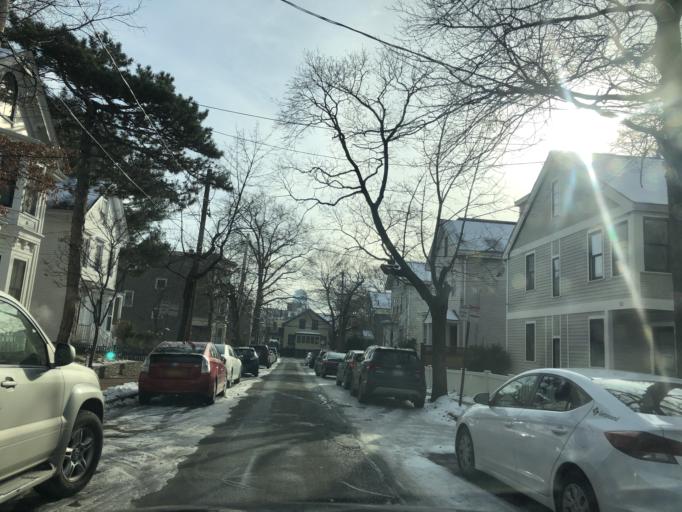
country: US
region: Massachusetts
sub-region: Middlesex County
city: Cambridge
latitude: 42.3621
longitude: -71.1069
